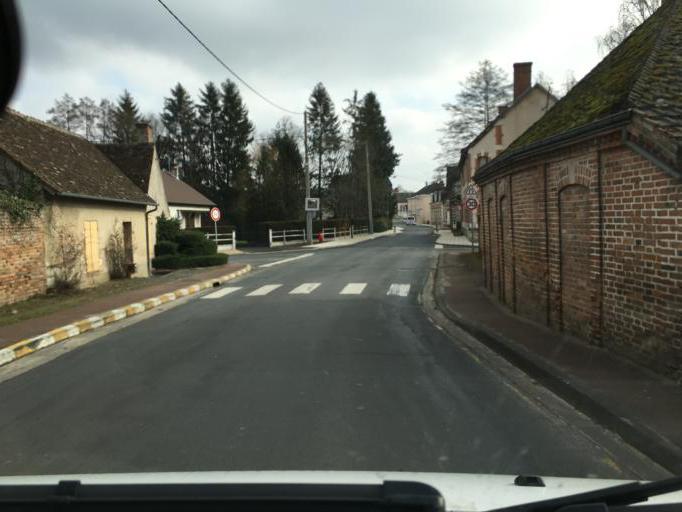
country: FR
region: Centre
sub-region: Departement du Loir-et-Cher
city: Neung-sur-Beuvron
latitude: 47.5359
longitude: 1.8025
